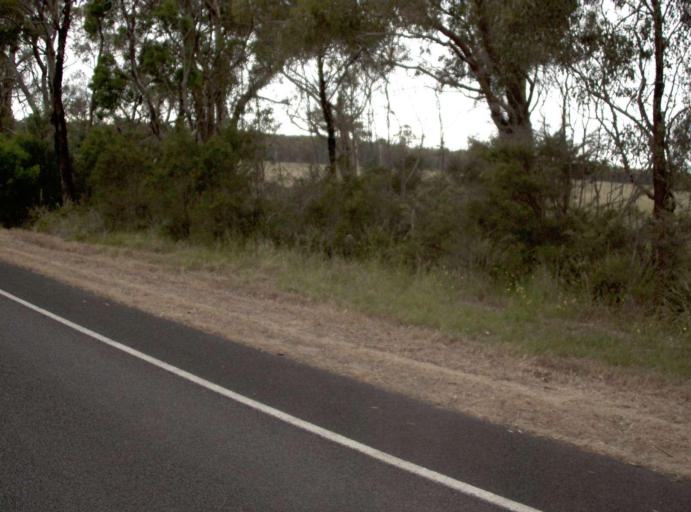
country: AU
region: Victoria
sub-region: Wellington
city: Sale
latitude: -38.4684
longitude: 146.9305
